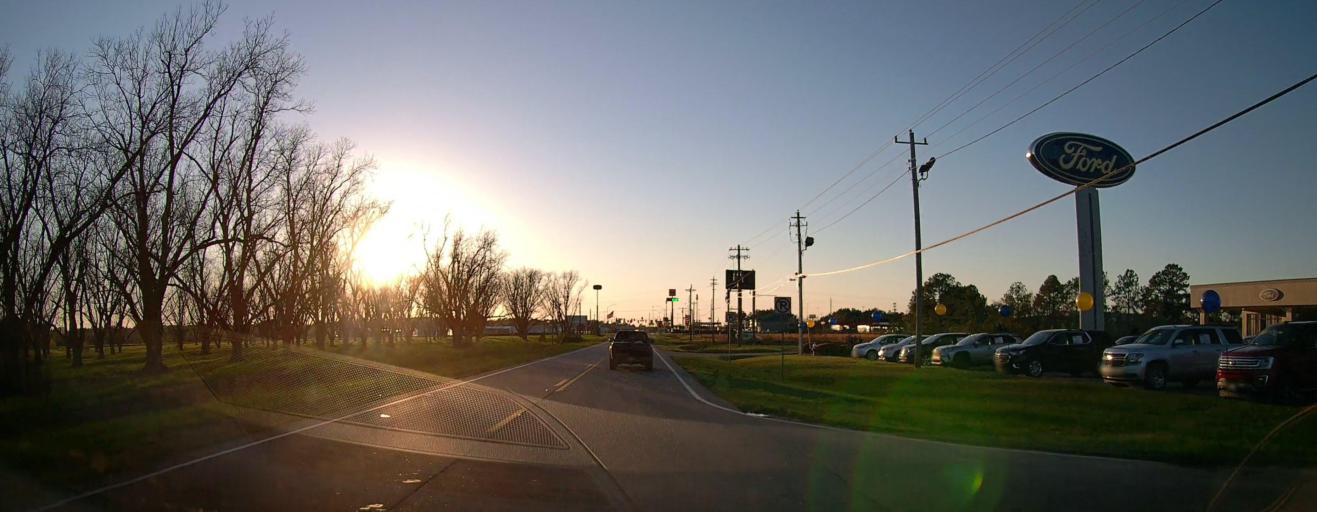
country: US
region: Georgia
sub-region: Crisp County
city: Cordele
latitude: 31.9583
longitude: -83.7422
